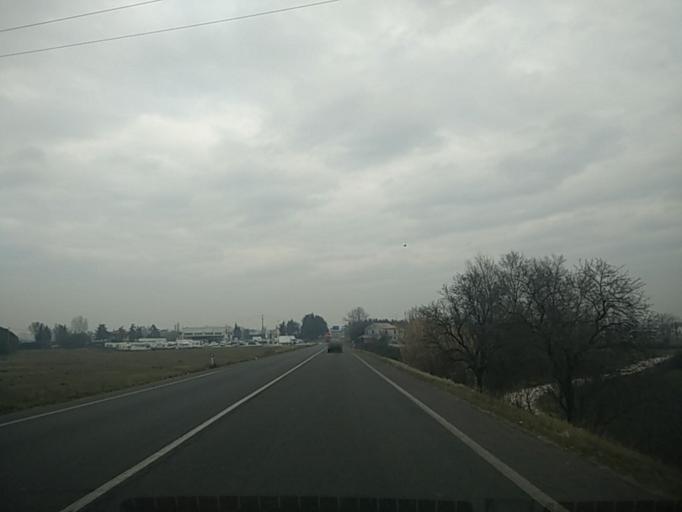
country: IT
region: Emilia-Romagna
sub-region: Provincia di Rimini
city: Santa Giustina
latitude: 44.0844
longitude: 12.4729
